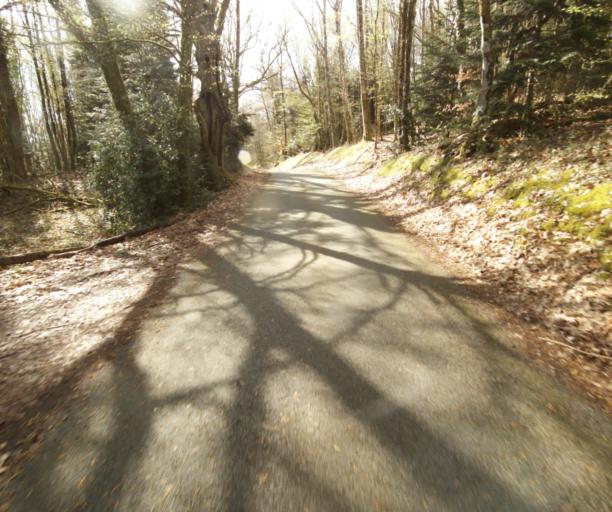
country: FR
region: Limousin
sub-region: Departement de la Correze
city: Laguenne
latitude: 45.2603
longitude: 1.8226
